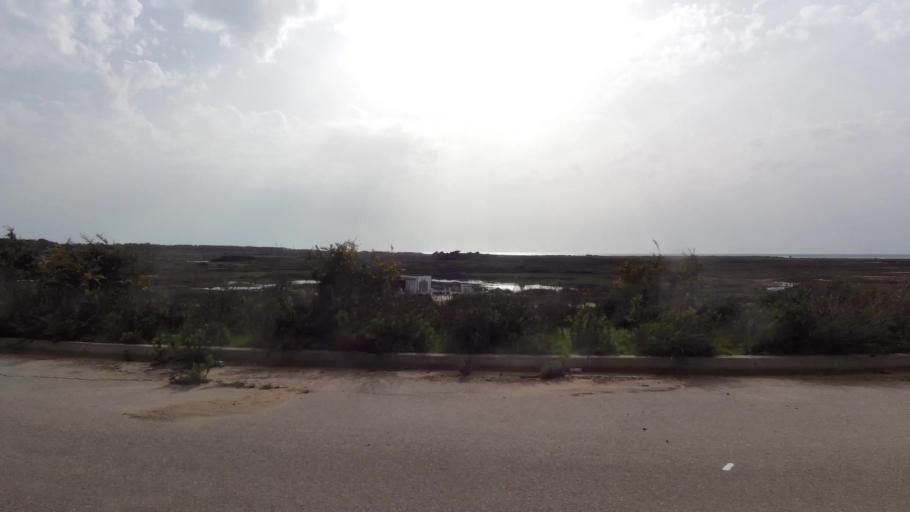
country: MA
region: Tanger-Tetouan
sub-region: Tanger-Assilah
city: Boukhalef
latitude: 35.6954
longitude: -5.9408
